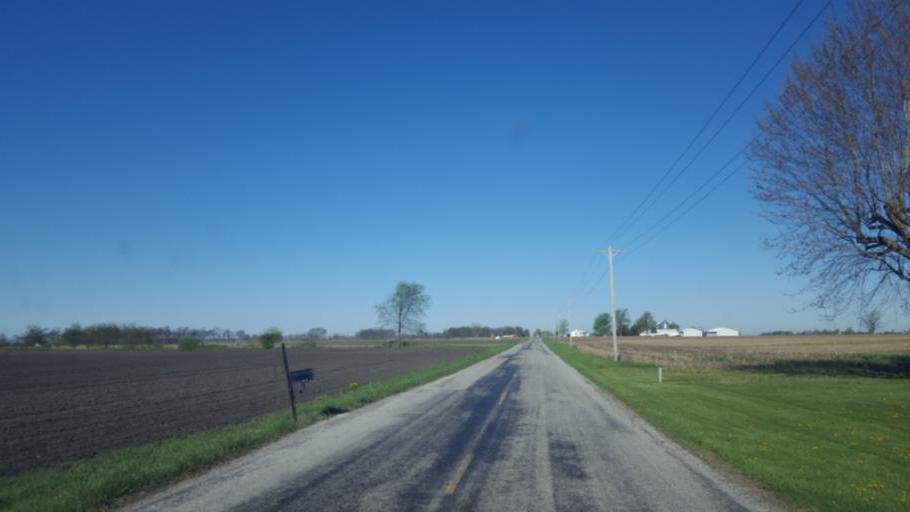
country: US
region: Ohio
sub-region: Crawford County
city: Bucyrus
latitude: 40.6743
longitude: -82.9847
